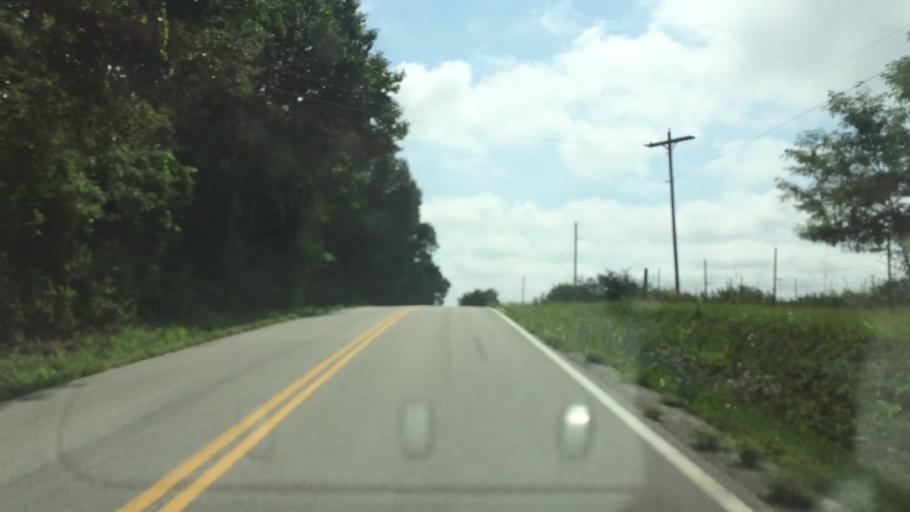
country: US
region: Missouri
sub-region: Greene County
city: Strafford
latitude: 37.2721
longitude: -93.1940
